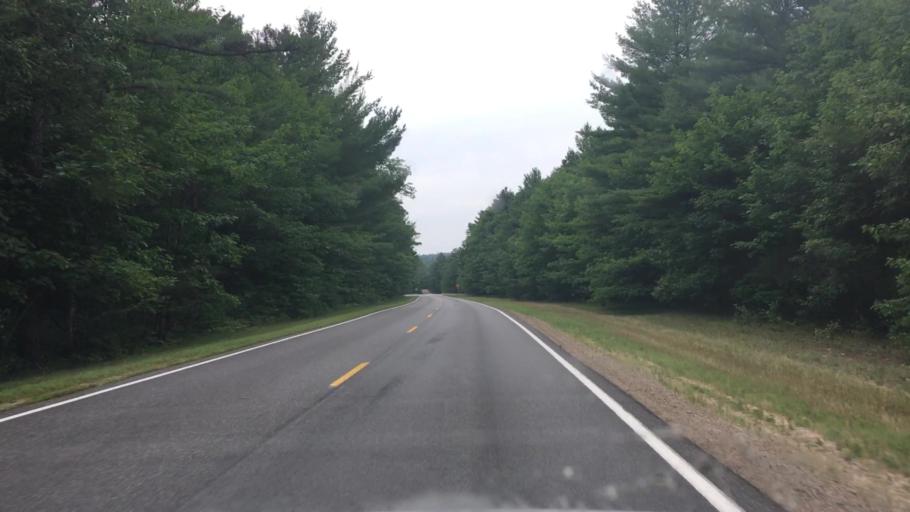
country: US
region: New York
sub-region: Clinton County
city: Morrisonville
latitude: 44.6219
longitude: -73.6131
